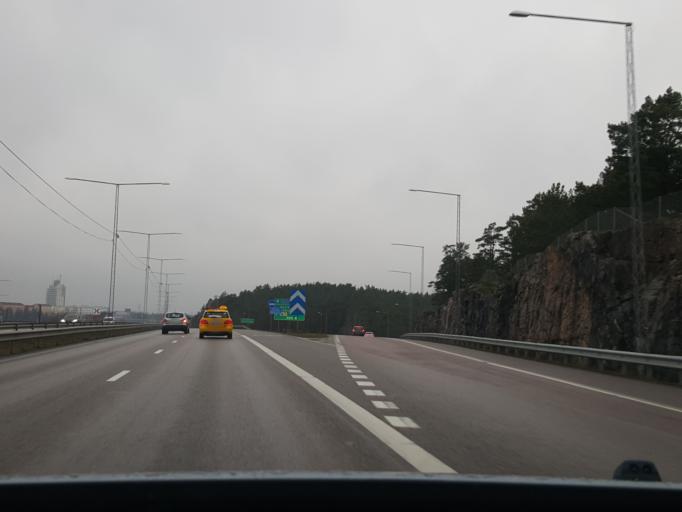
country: SE
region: Stockholm
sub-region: Nacka Kommun
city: Nacka
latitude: 59.3154
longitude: 18.1893
